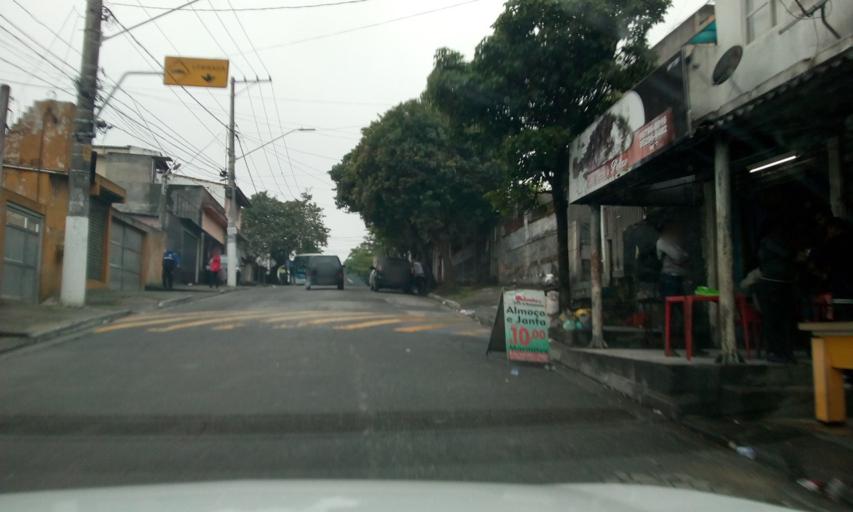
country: BR
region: Sao Paulo
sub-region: Diadema
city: Diadema
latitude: -23.7027
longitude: -46.6283
